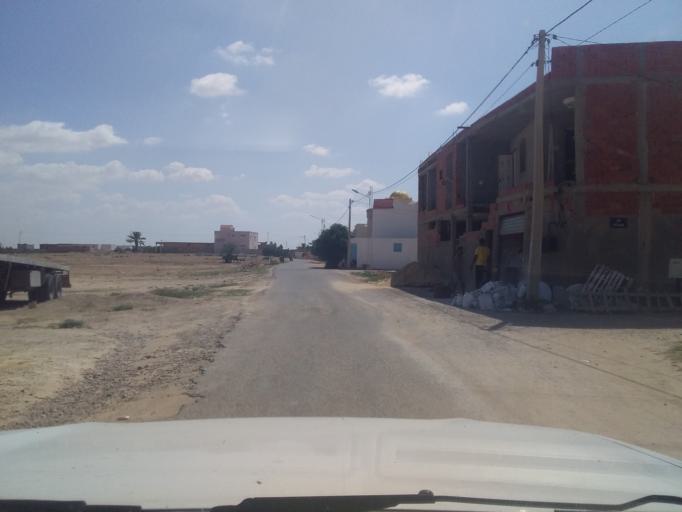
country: TN
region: Madanin
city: Medenine
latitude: 33.6139
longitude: 10.2975
